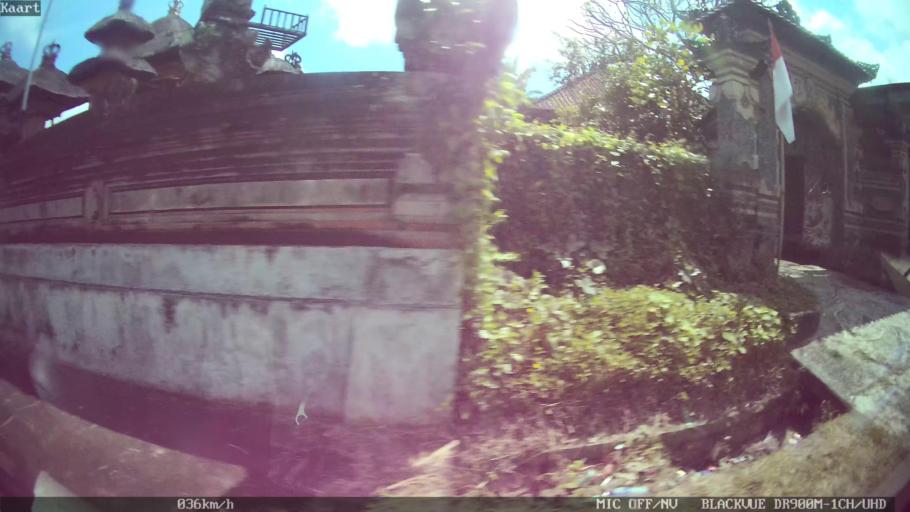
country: ID
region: Bali
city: Banjar Apuan Kaja
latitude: -8.5040
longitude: 115.3384
